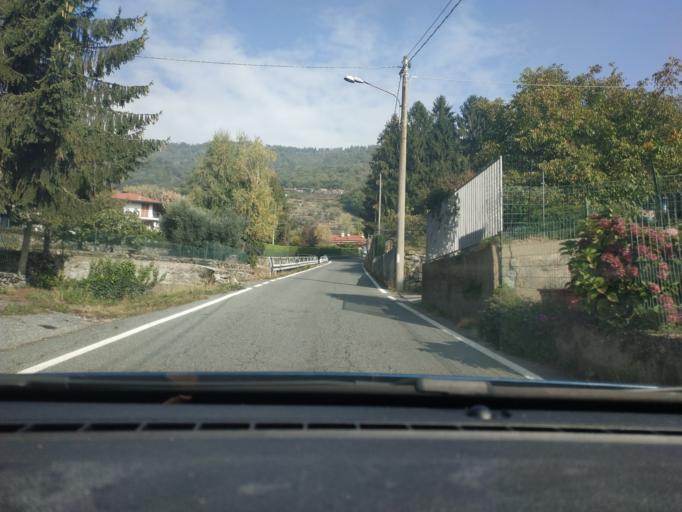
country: IT
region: Piedmont
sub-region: Provincia di Torino
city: Chiaverano
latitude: 45.5022
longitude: 7.9079
